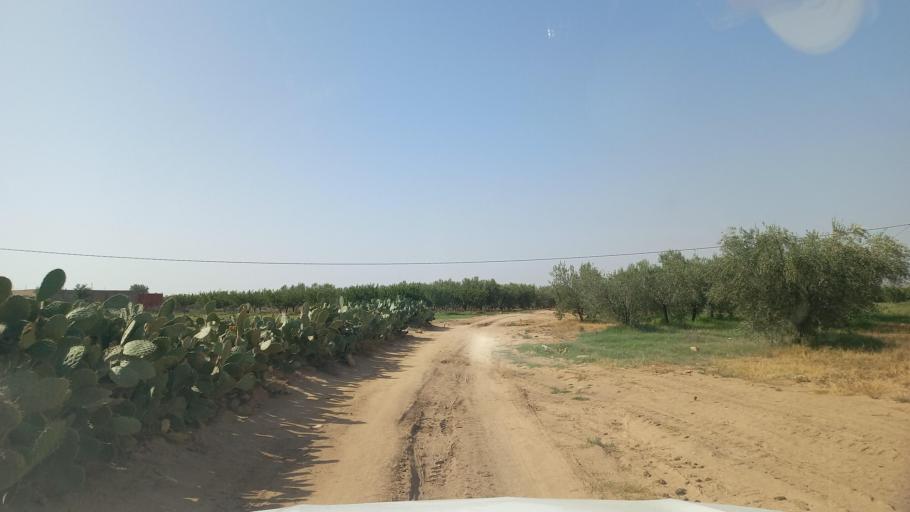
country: TN
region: Al Qasrayn
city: Kasserine
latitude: 35.2540
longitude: 9.0448
